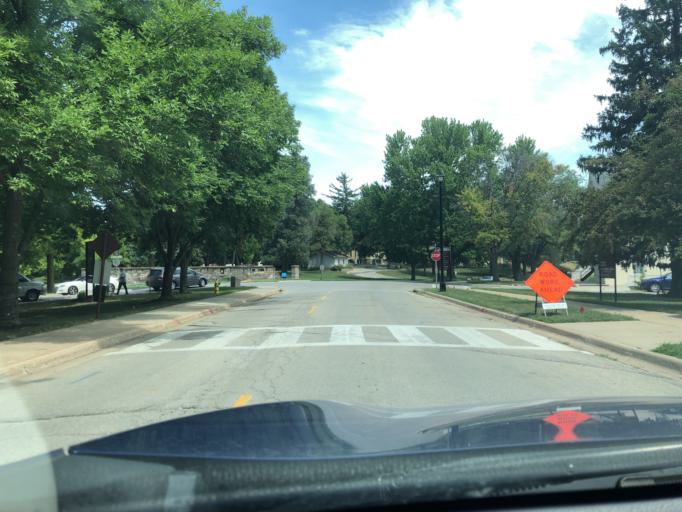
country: US
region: Kansas
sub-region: Leavenworth County
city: Leavenworth
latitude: 39.3549
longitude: -94.9166
